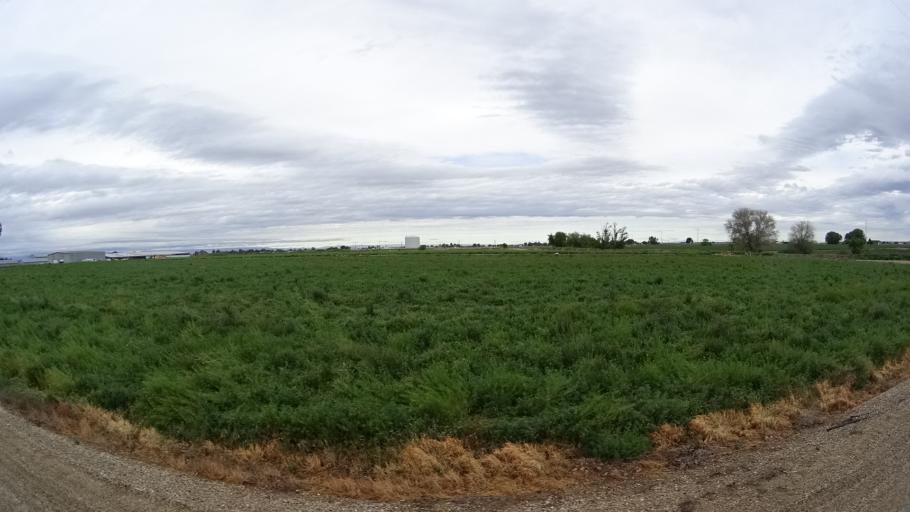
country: US
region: Idaho
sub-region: Ada County
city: Star
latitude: 43.6436
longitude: -116.4935
